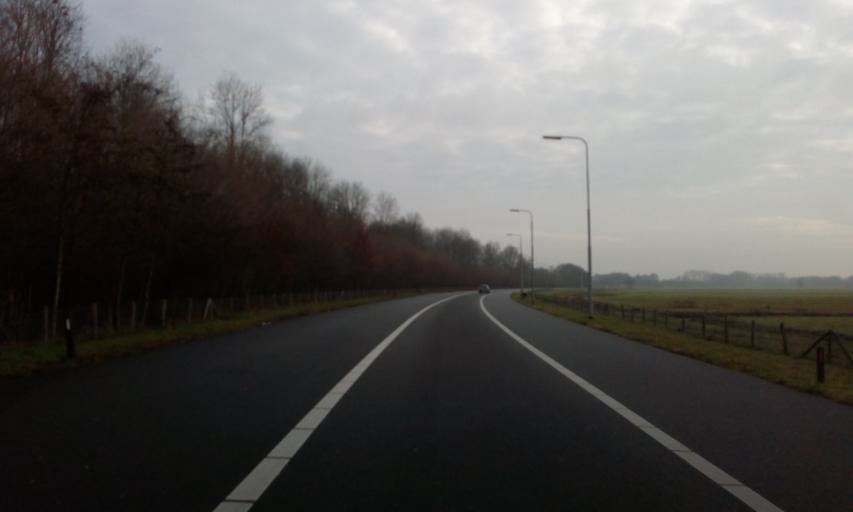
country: NL
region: North Holland
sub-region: Gemeente Naarden
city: Naarden
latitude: 52.3049
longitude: 5.1346
